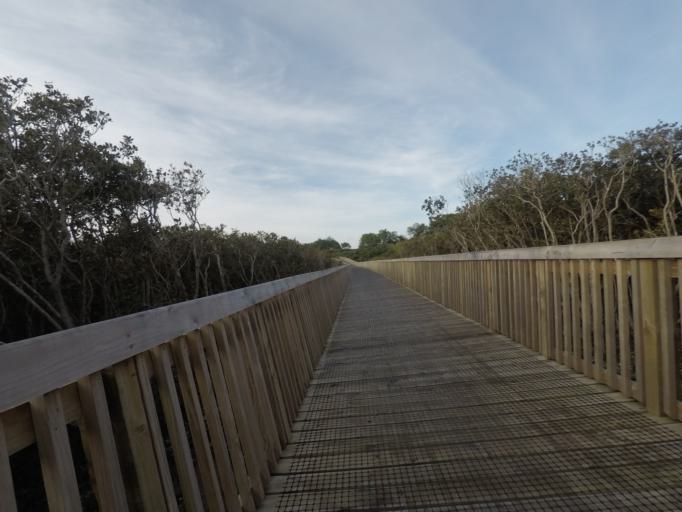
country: NZ
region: Auckland
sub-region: Auckland
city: Mangere
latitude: -36.9480
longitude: 174.8003
